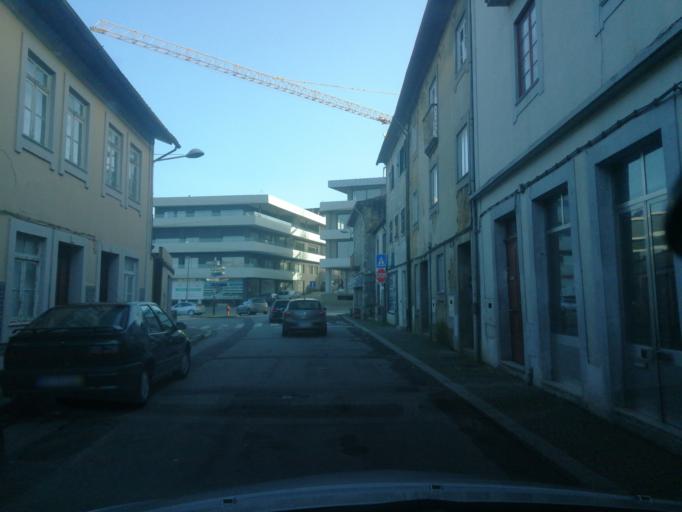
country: PT
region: Braga
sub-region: Barcelos
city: Barcelos
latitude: 41.5263
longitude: -8.6211
